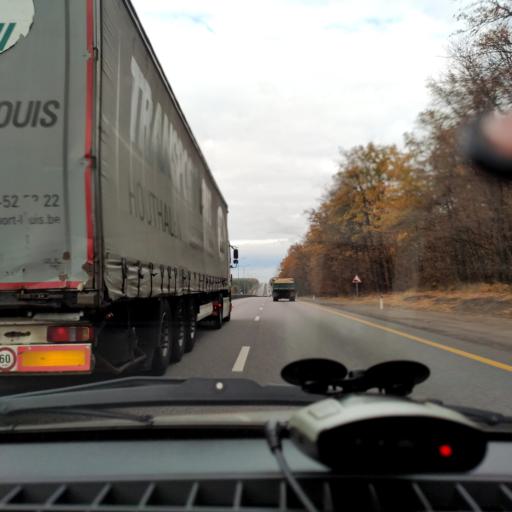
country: RU
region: Voronezj
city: Ramon'
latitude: 51.8607
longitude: 39.2158
